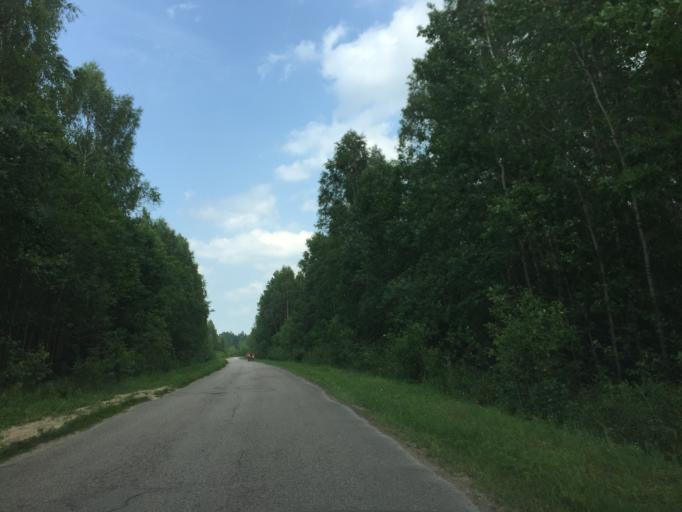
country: LV
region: Olaine
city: Olaine
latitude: 56.7806
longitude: 23.8751
